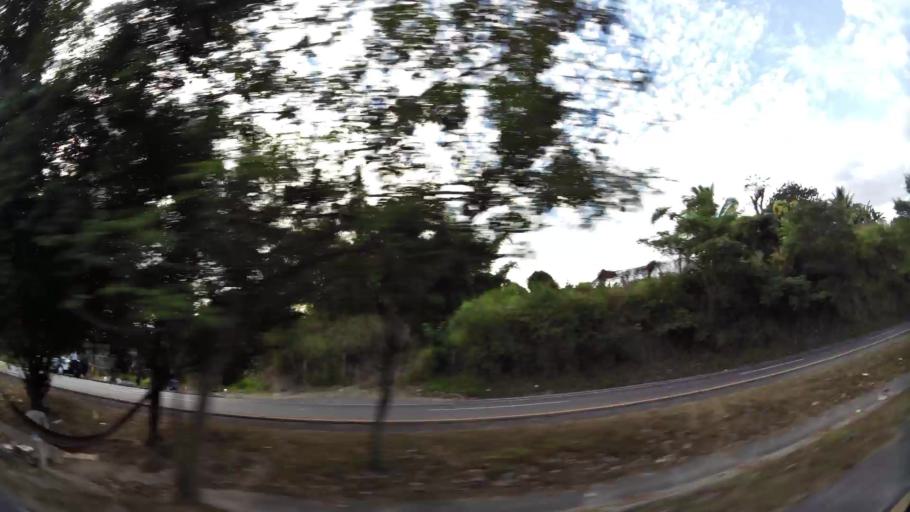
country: SV
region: Cuscatlan
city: Cojutepeque
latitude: 13.7261
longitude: -88.9000
